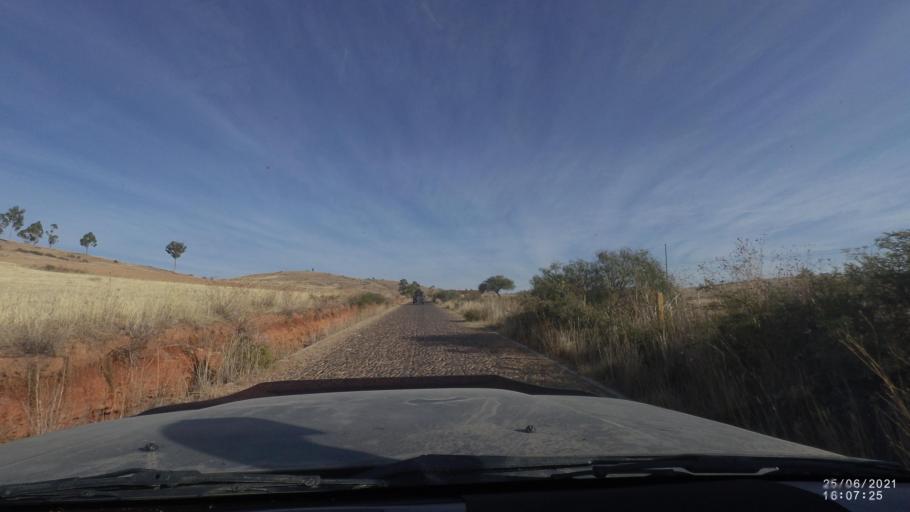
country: BO
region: Cochabamba
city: Cliza
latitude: -17.6738
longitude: -65.9036
